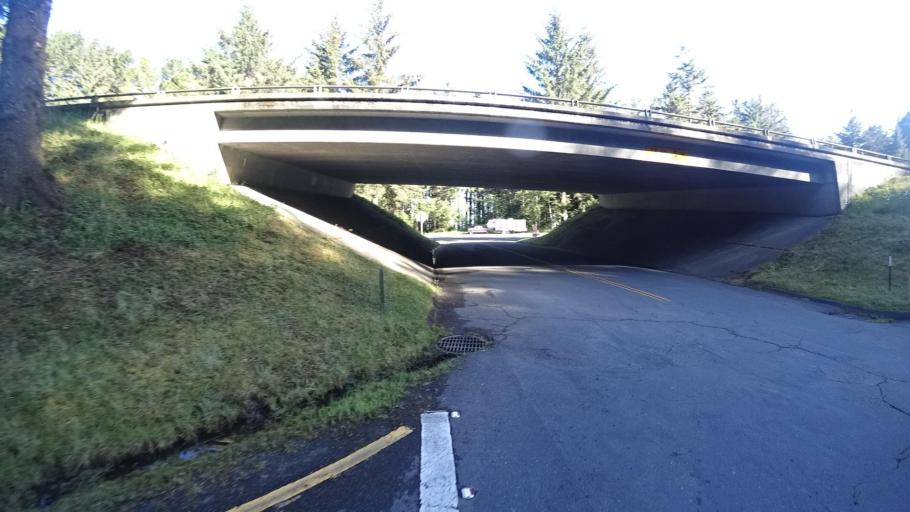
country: US
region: California
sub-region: Humboldt County
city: Westhaven-Moonstone
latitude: 41.1360
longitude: -124.1466
